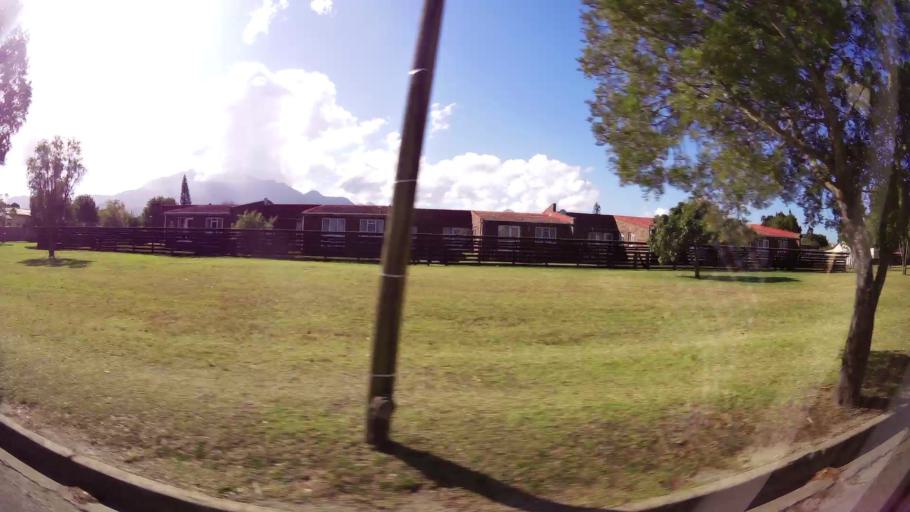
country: ZA
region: Western Cape
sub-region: Eden District Municipality
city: George
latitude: -33.9744
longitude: 22.4514
